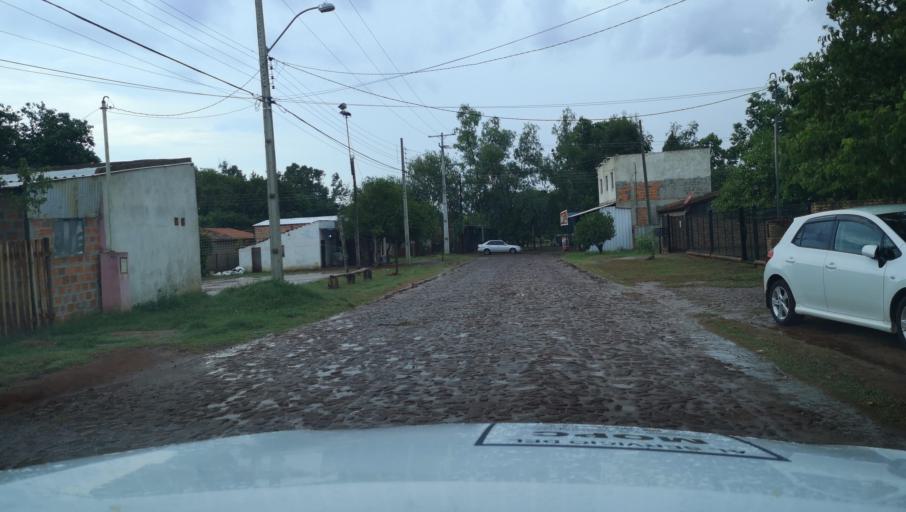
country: PY
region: Misiones
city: Santa Maria
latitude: -26.8958
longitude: -57.0318
